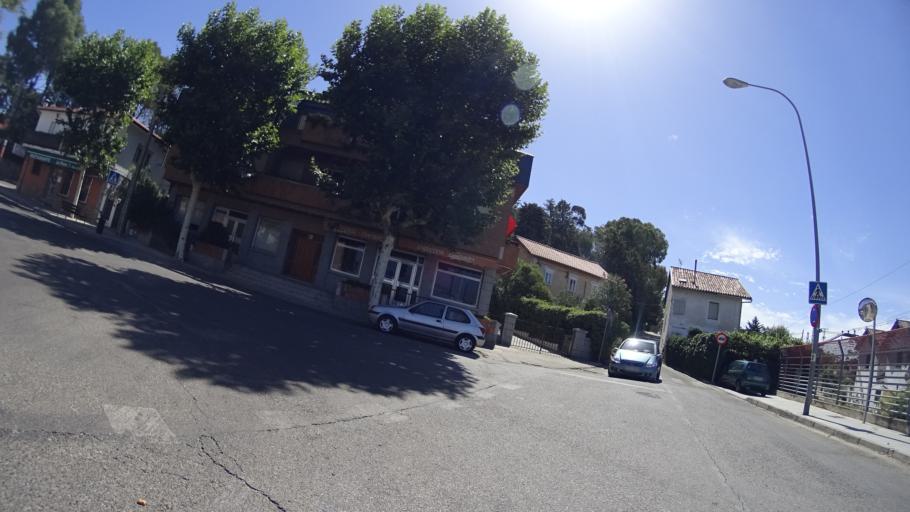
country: ES
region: Madrid
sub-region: Provincia de Madrid
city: Torrelodones
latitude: 40.5728
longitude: -3.9542
